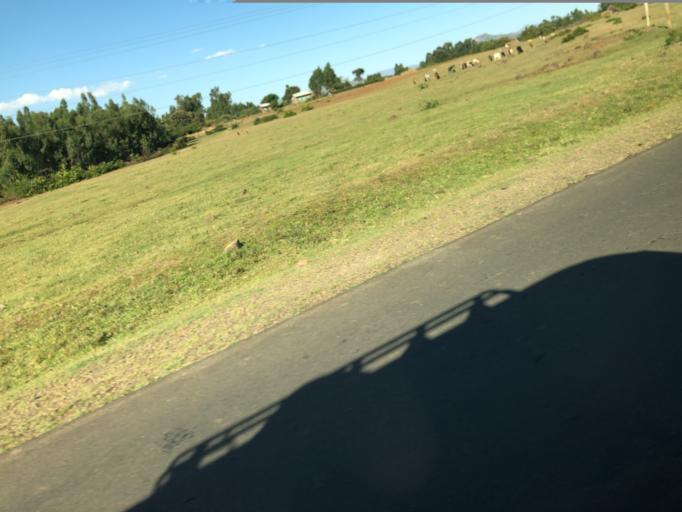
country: ET
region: Amhara
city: Werota
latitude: 11.9310
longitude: 37.8372
